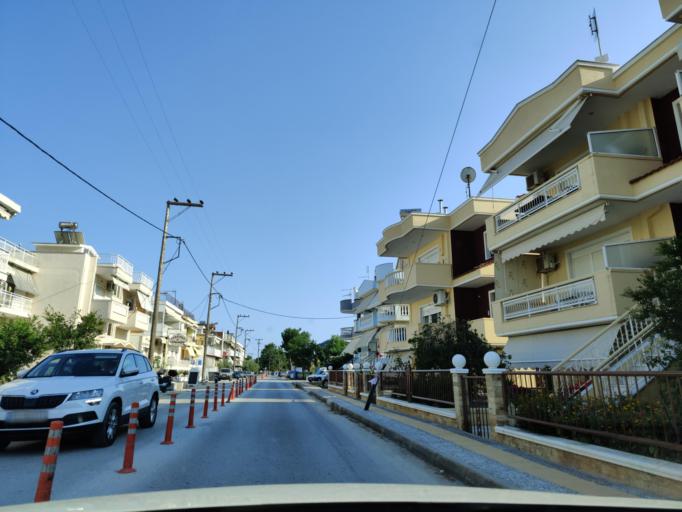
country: GR
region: East Macedonia and Thrace
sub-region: Nomos Kavalas
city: Nea Peramos
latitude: 40.8323
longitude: 24.3045
